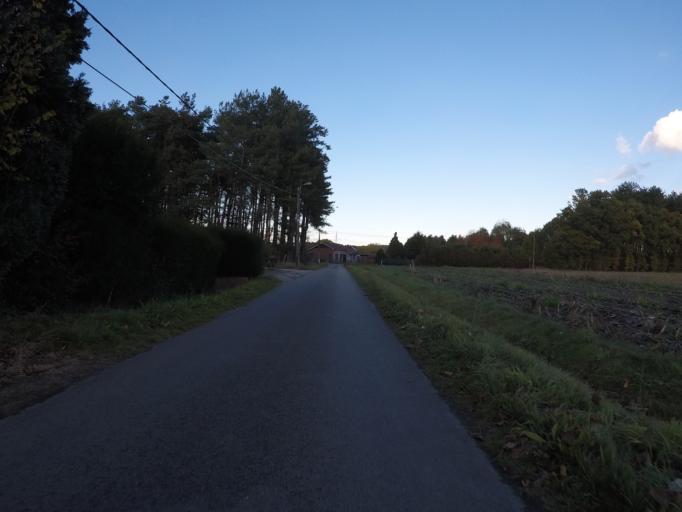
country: BE
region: Flanders
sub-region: Provincie Vlaams-Brabant
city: Begijnendijk
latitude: 51.0039
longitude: 4.8102
